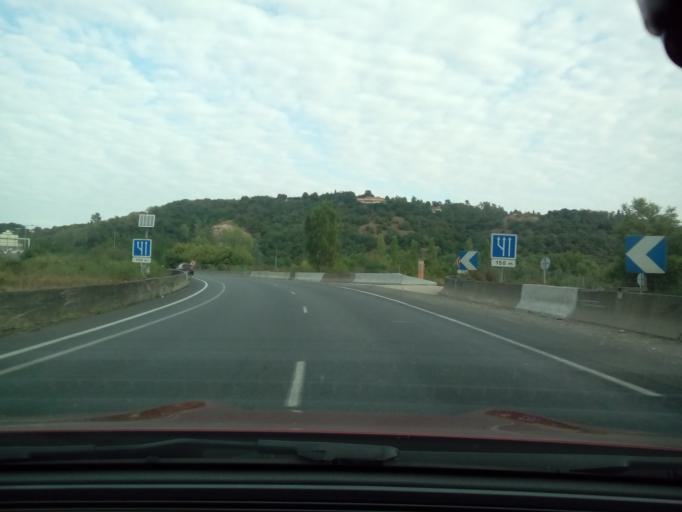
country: FR
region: Rhone-Alpes
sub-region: Departement du Rhone
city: Vaulx-en-Velin
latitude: 45.8048
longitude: 4.9258
